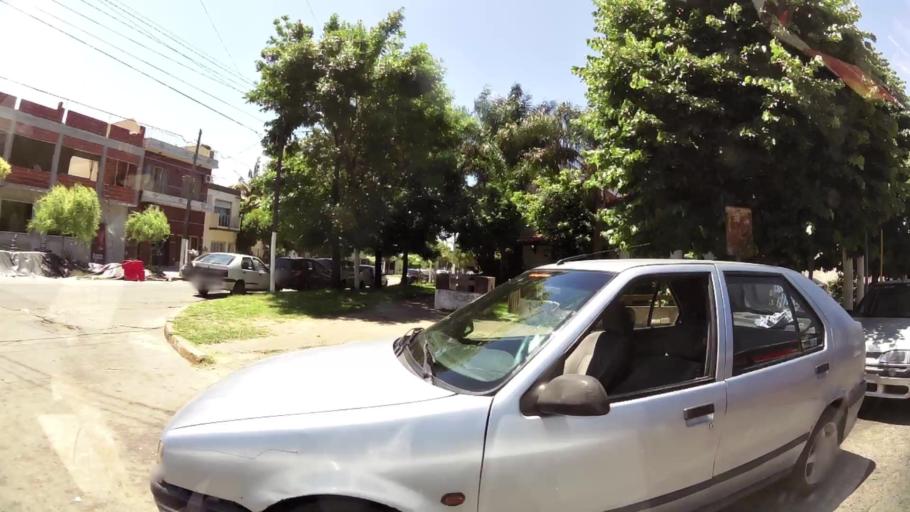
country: AR
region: Buenos Aires
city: Caseros
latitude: -34.5889
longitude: -58.5710
